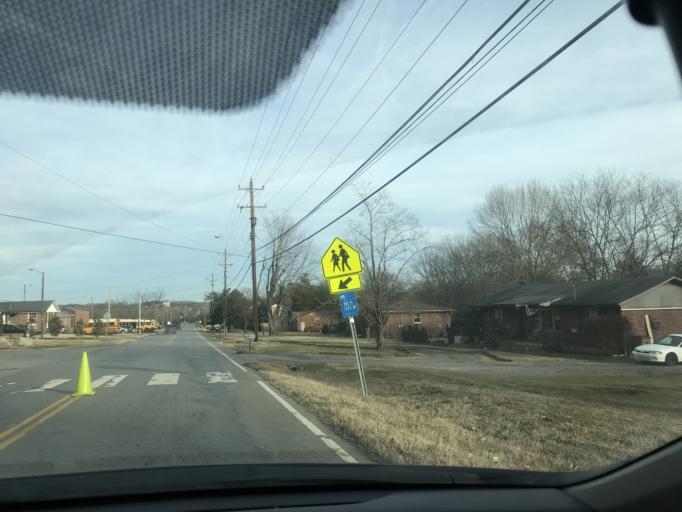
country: US
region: Tennessee
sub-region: Davidson County
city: Nashville
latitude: 36.2194
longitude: -86.8292
